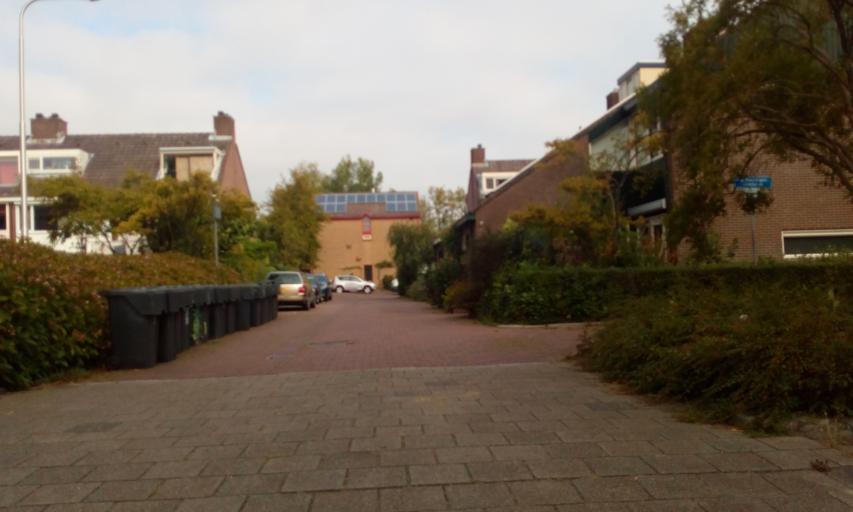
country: NL
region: South Holland
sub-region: Gemeente Voorschoten
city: Voorschoten
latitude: 52.1449
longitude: 4.4589
